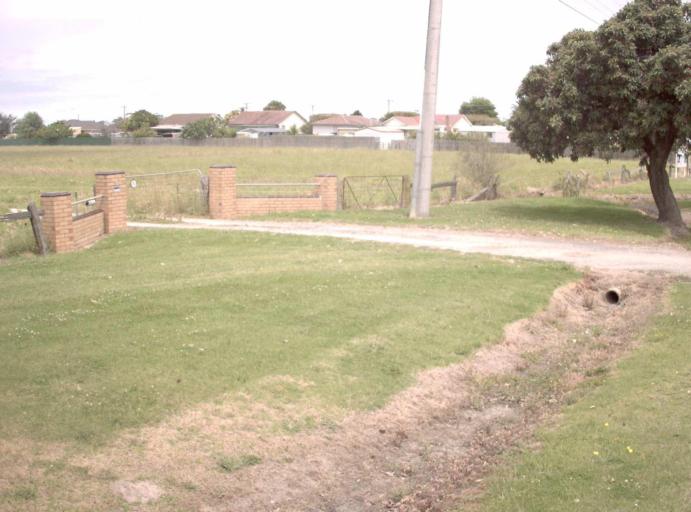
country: AU
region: Victoria
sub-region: Latrobe
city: Traralgon
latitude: -38.5532
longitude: 146.6805
